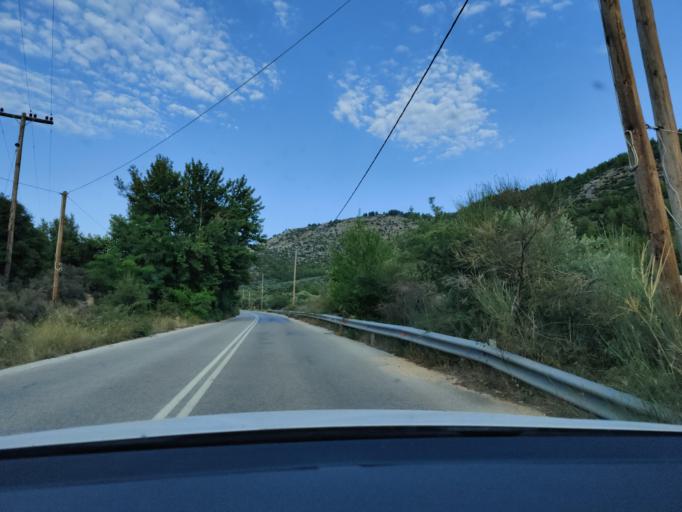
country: GR
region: East Macedonia and Thrace
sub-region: Nomos Kavalas
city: Limenaria
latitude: 40.6134
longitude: 24.6311
